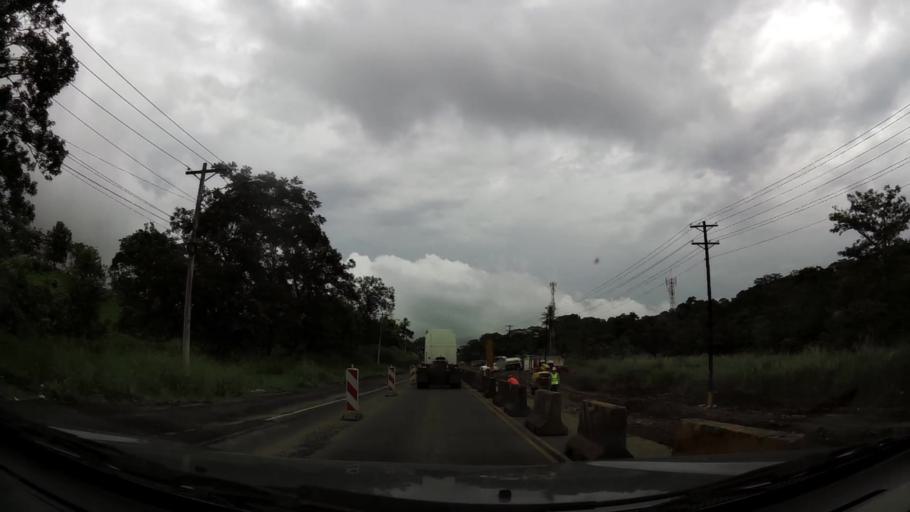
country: PA
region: Colon
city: Nuevo Vigia
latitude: 9.2131
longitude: -79.6260
